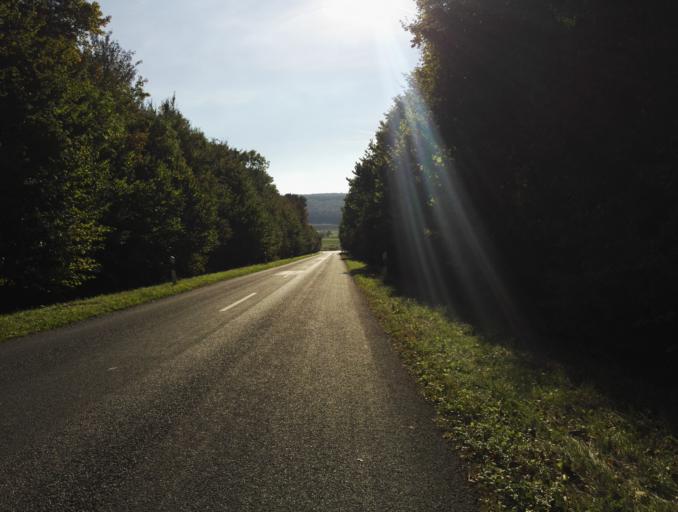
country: DE
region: Lower Saxony
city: Holle
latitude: 52.1090
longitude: 10.1128
